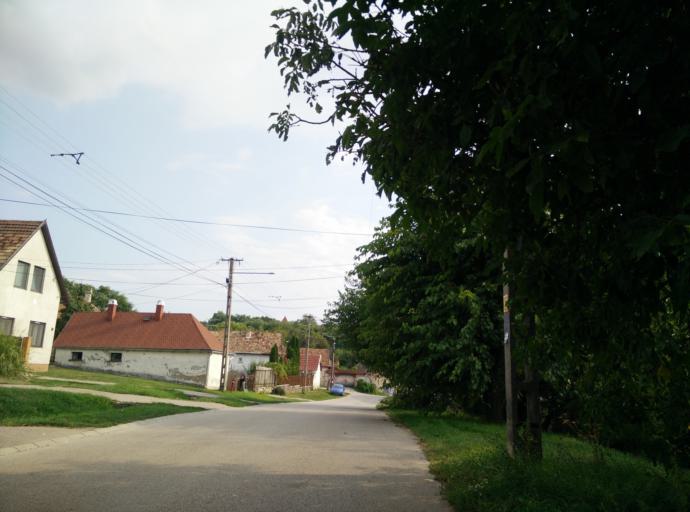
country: HU
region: Pest
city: Paty
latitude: 47.5137
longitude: 18.8335
